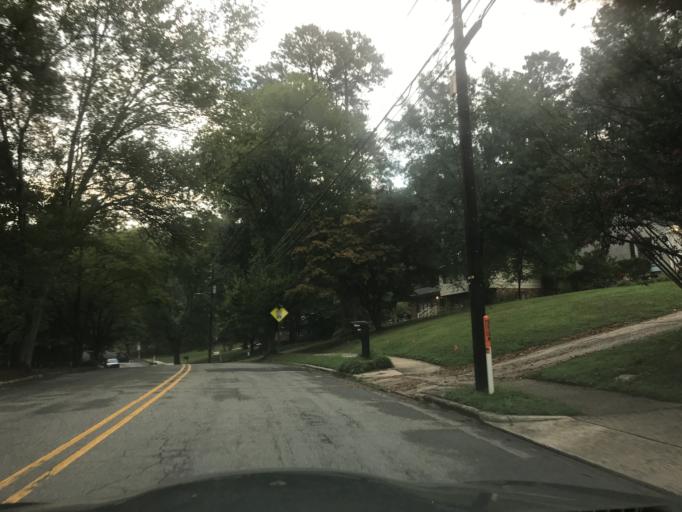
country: US
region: North Carolina
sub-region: Wake County
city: West Raleigh
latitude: 35.8436
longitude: -78.6594
